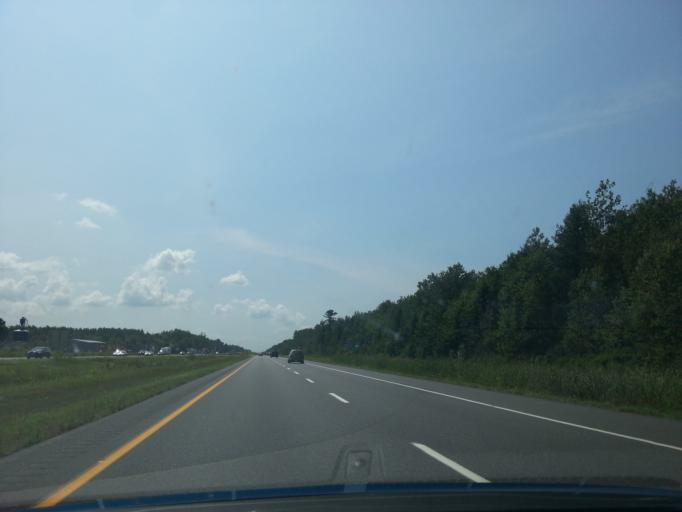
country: CA
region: Quebec
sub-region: Mauricie
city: Daveluyville
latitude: 46.2118
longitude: -72.0652
